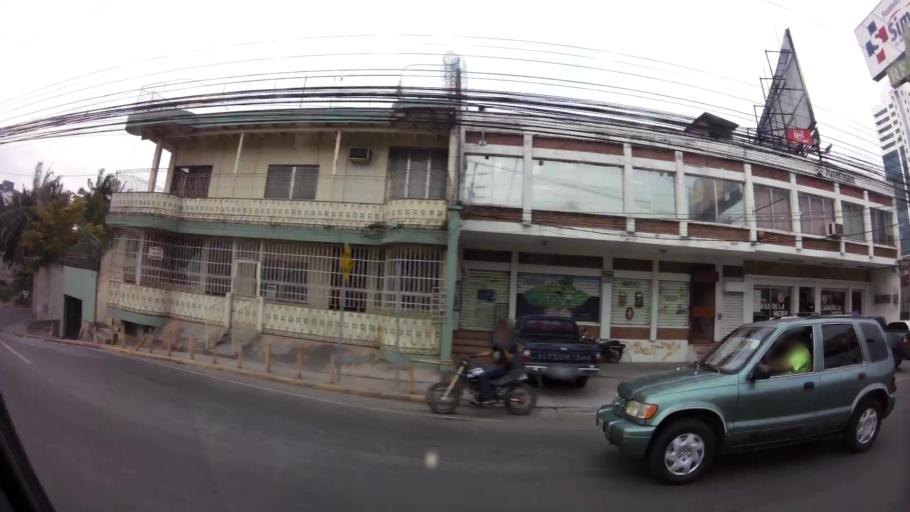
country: HN
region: Francisco Morazan
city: Tegucigalpa
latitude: 14.1003
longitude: -87.1844
